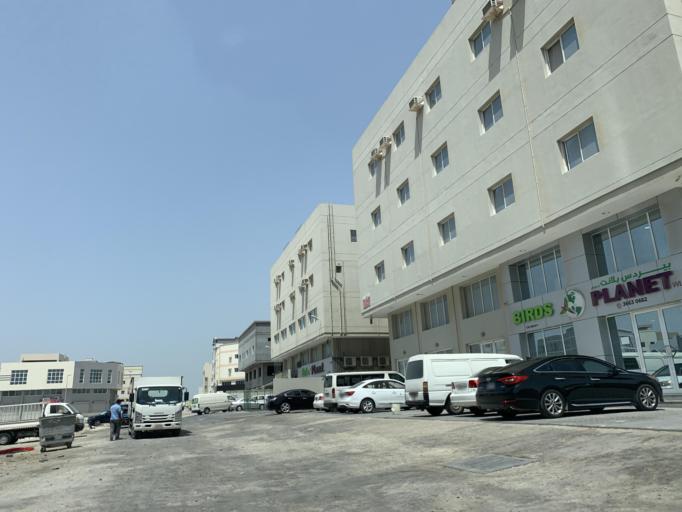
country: BH
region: Northern
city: Madinat `Isa
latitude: 26.1901
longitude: 50.5487
